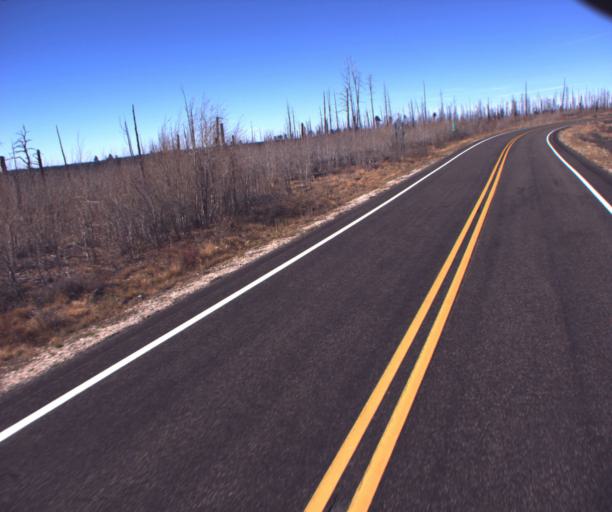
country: US
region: Arizona
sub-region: Coconino County
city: Fredonia
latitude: 36.5870
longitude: -112.1776
